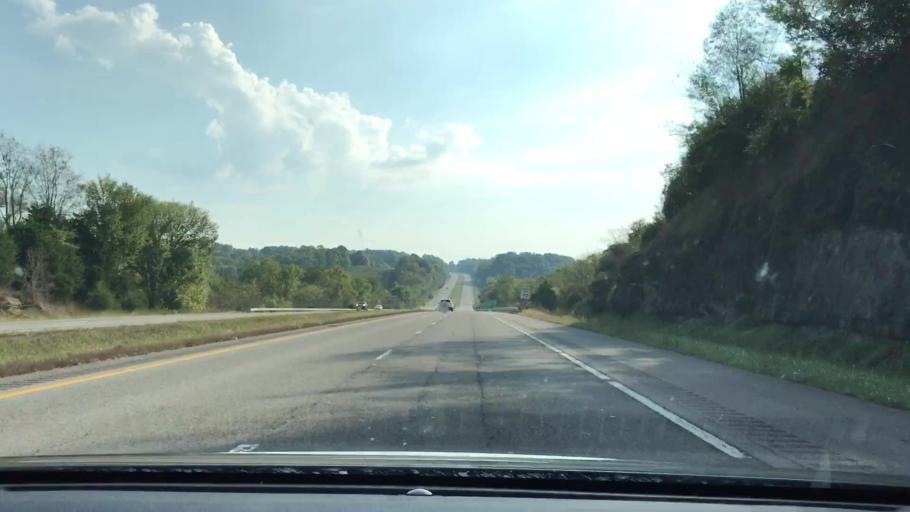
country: US
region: Kentucky
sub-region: Metcalfe County
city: Edmonton
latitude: 36.9960
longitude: -85.6512
